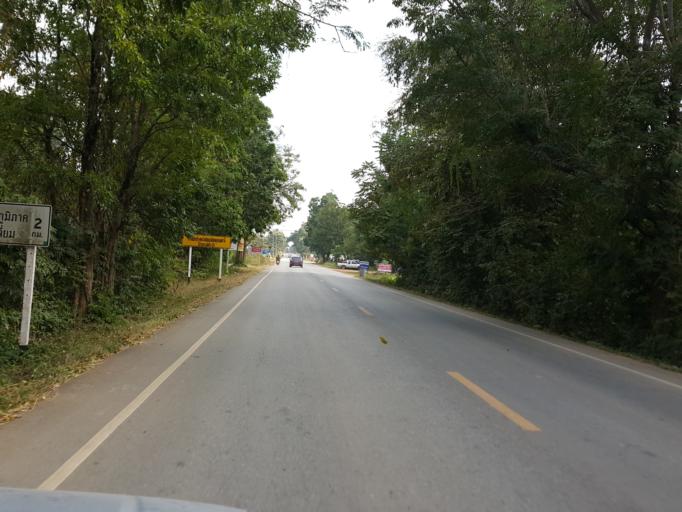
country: TH
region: Sukhothai
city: Thung Saliam
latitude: 17.3334
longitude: 99.5478
